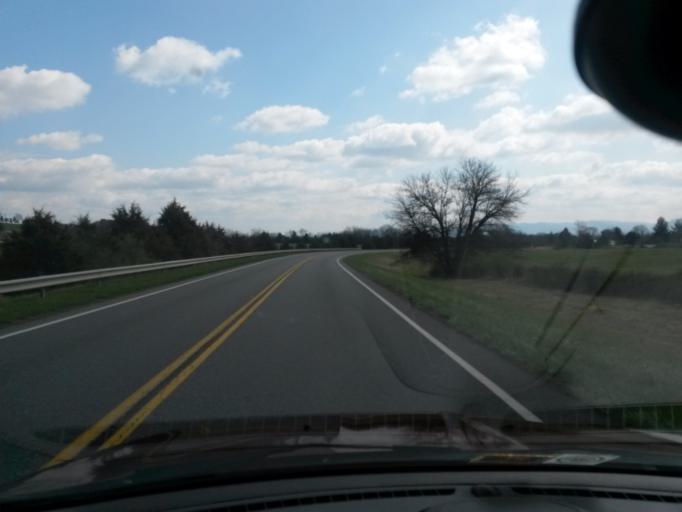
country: US
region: Virginia
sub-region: Augusta County
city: Weyers Cave
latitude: 38.2886
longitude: -78.9245
